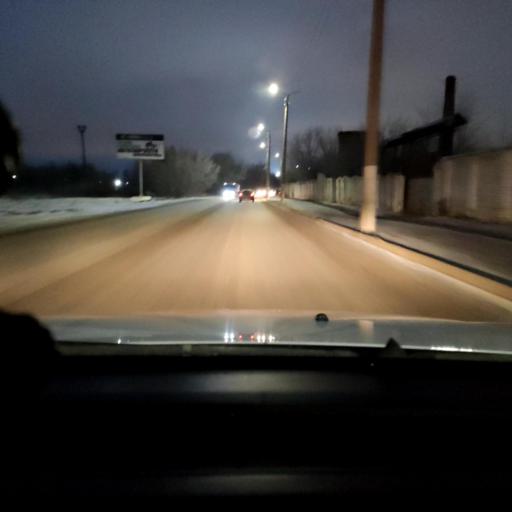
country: RU
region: Samara
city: Chapayevsk
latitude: 52.9669
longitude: 49.6942
